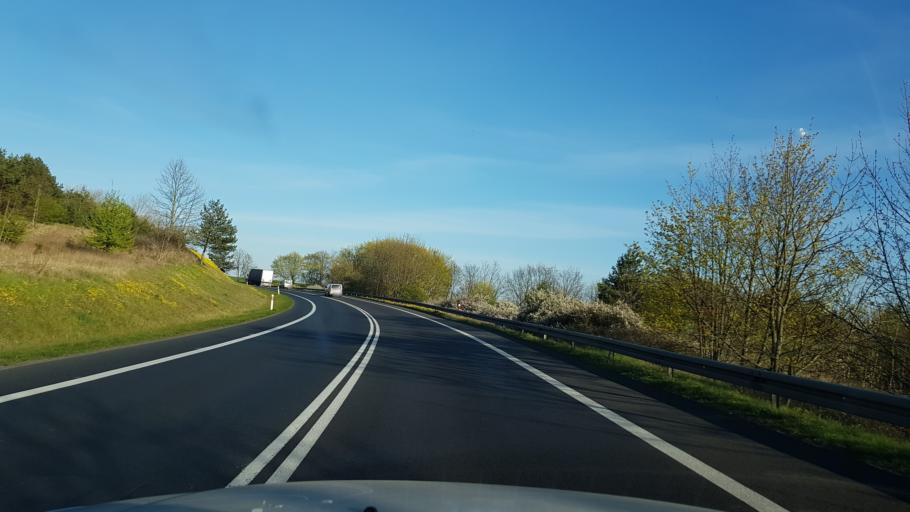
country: PL
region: West Pomeranian Voivodeship
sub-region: Powiat kamienski
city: Wolin
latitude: 53.8616
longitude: 14.5577
